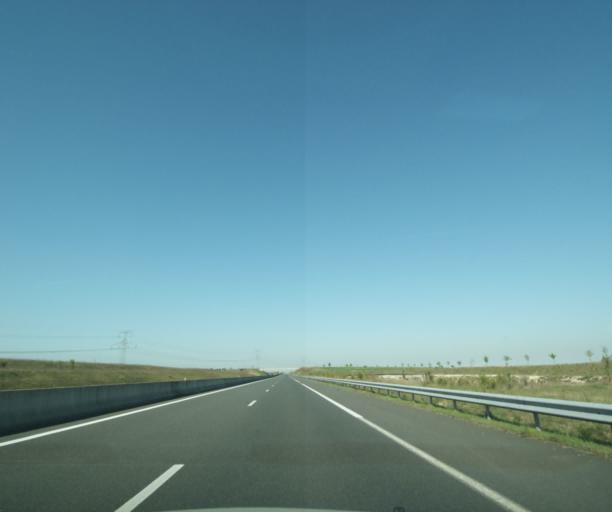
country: FR
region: Centre
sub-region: Departement du Loiret
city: Dadonville
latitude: 48.1131
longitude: 2.2536
